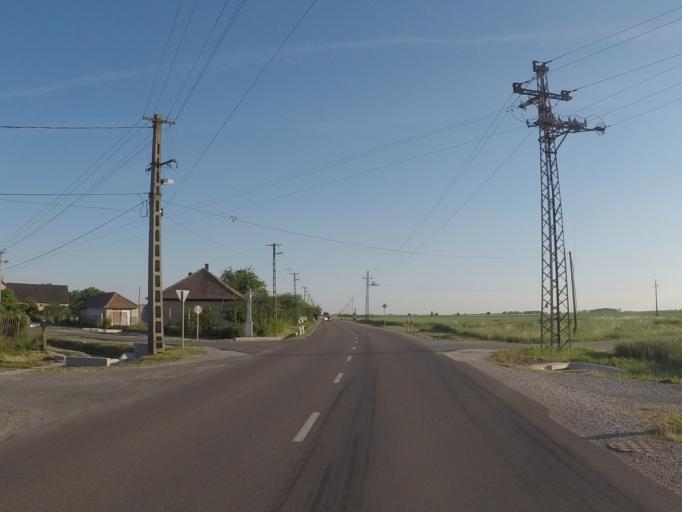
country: HU
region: Heves
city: Besenyotelek
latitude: 47.7191
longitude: 20.4145
